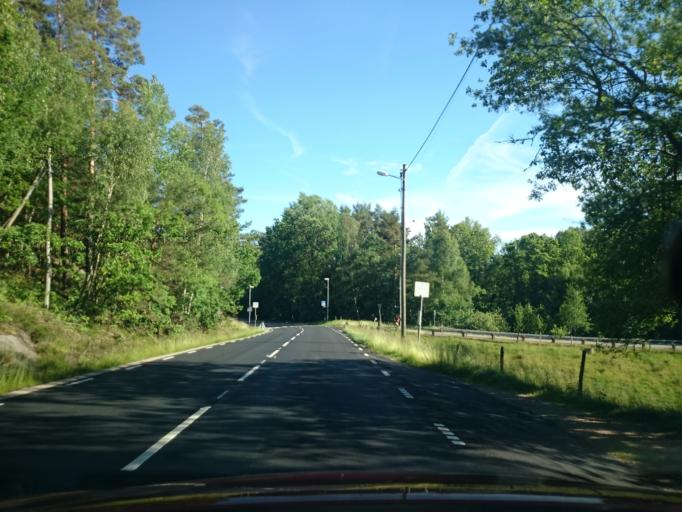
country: SE
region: Vaestra Goetaland
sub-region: Lerums Kommun
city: Lerum
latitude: 57.7788
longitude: 12.2545
